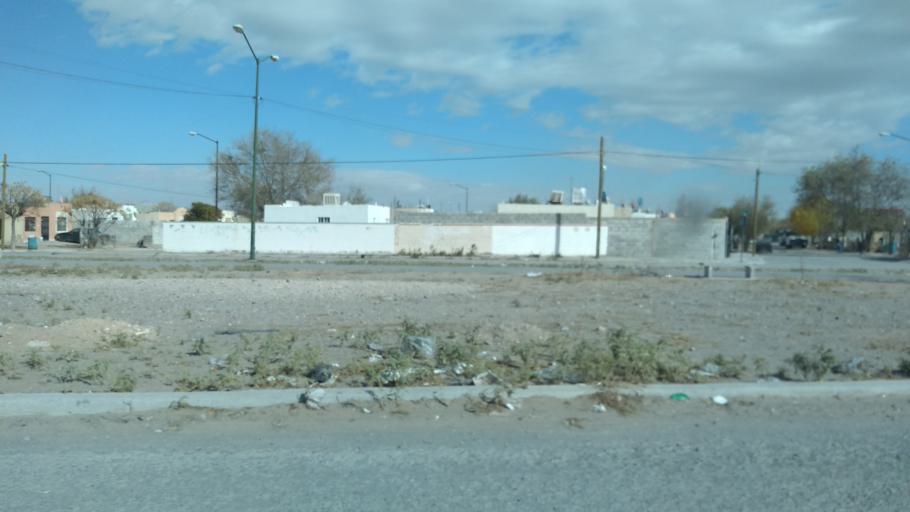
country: US
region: Texas
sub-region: El Paso County
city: San Elizario
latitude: 31.5841
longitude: -106.3530
